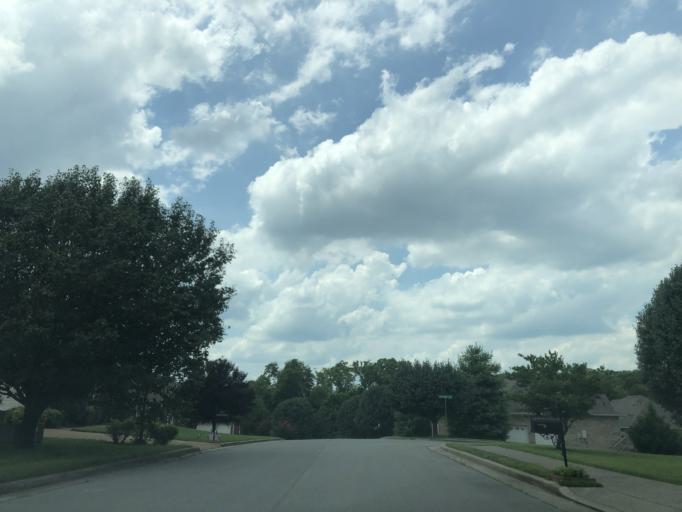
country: US
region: Tennessee
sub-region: Williamson County
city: Brentwood Estates
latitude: 36.0254
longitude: -86.7332
